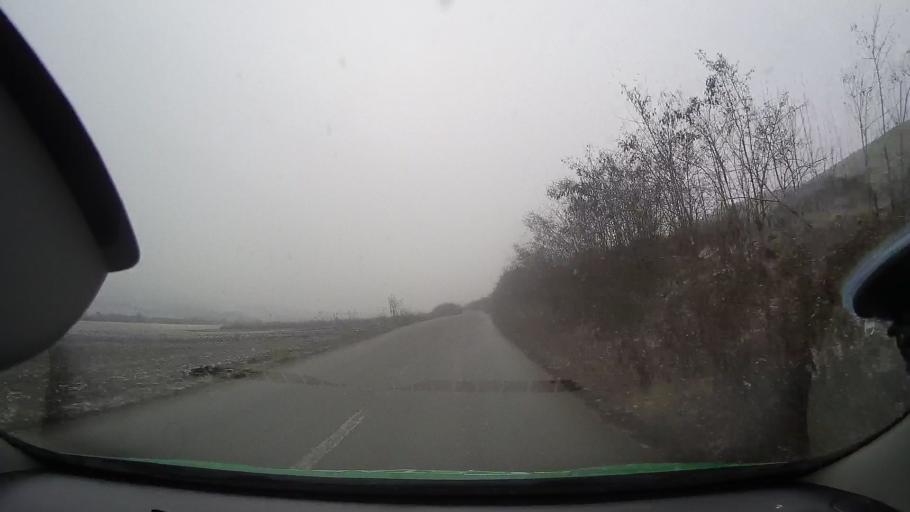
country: RO
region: Alba
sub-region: Comuna Noslac
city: Noslac
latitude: 46.3689
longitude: 23.9276
